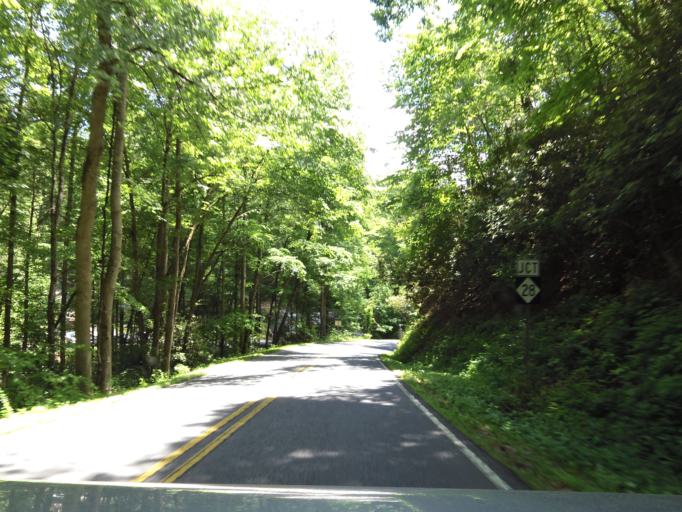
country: US
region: North Carolina
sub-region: Graham County
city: Robbinsville
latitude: 35.4686
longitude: -83.9207
